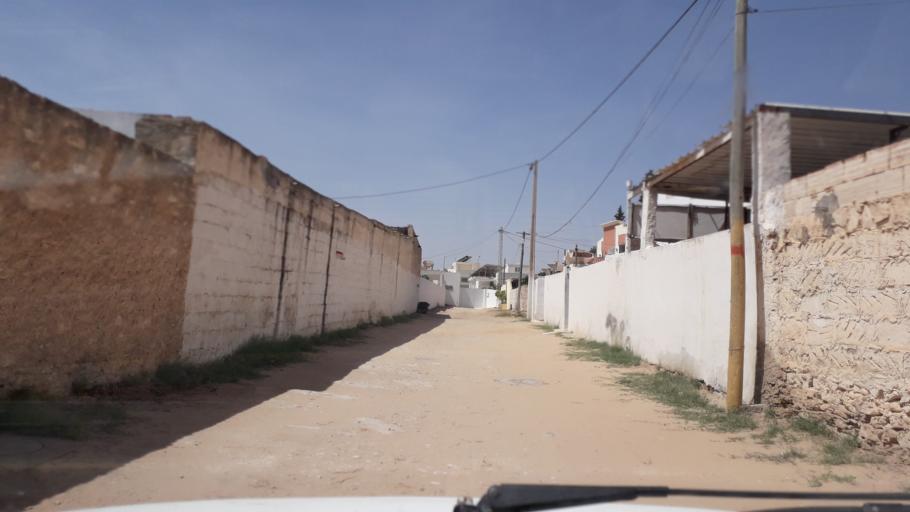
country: TN
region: Safaqis
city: Al Qarmadah
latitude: 34.7994
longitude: 10.7688
